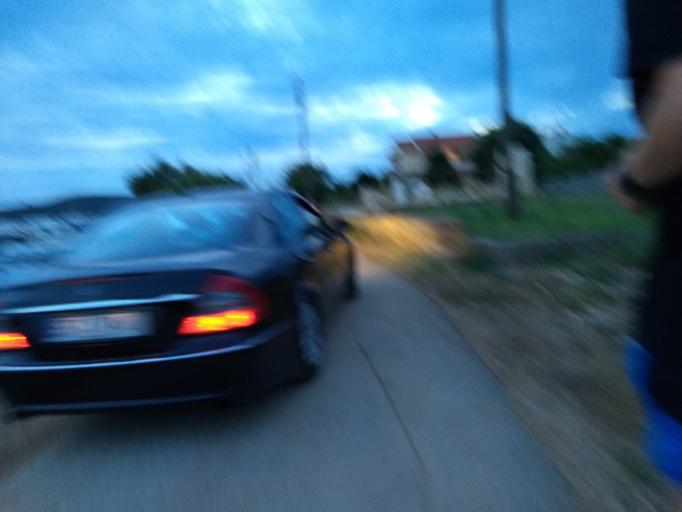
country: HR
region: Zadarska
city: Ugljan
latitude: 44.1392
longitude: 15.0727
